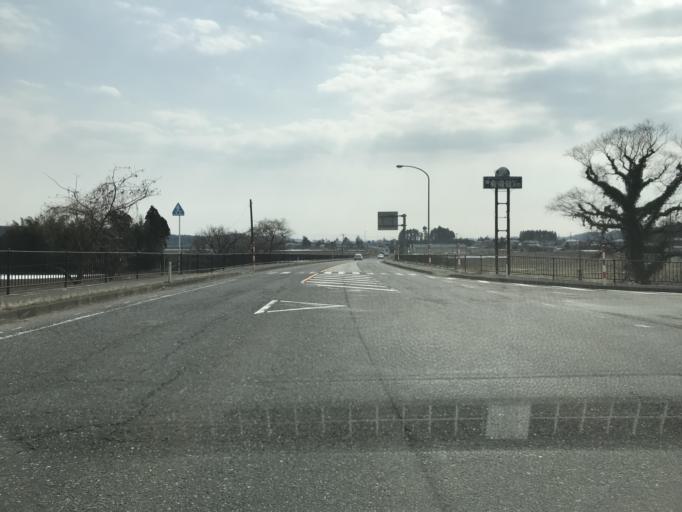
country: JP
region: Miyagi
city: Furukawa
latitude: 38.6767
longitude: 140.8614
